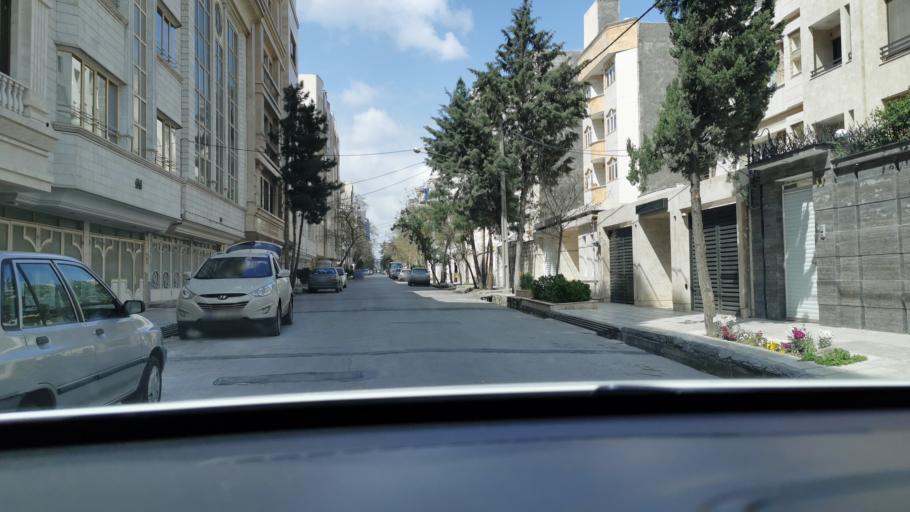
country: IR
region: Razavi Khorasan
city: Mashhad
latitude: 36.3218
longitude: 59.5309
